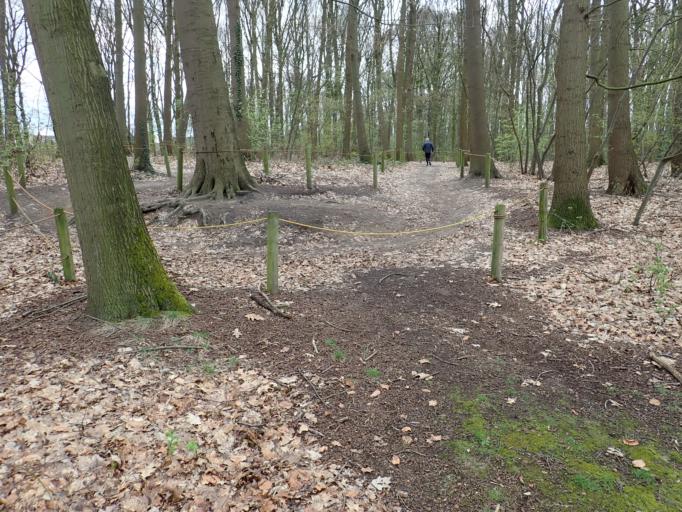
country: BE
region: Flanders
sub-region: Provincie Antwerpen
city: Vorselaar
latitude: 51.2057
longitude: 4.7723
